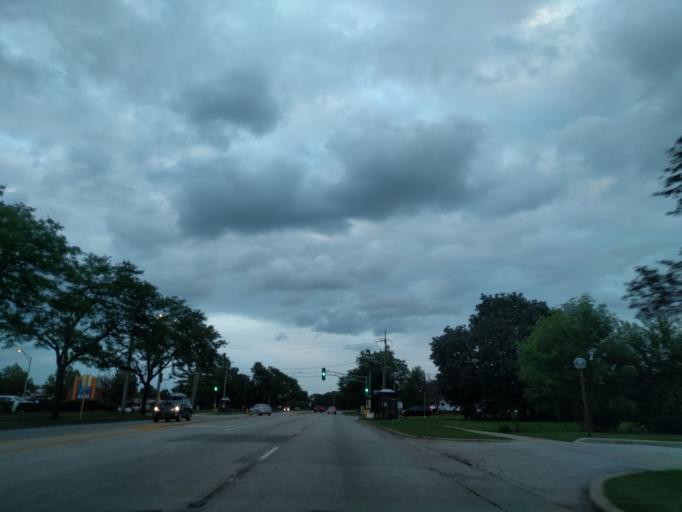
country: US
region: Illinois
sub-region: Cook County
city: Arlington Heights
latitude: 42.0513
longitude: -87.9759
